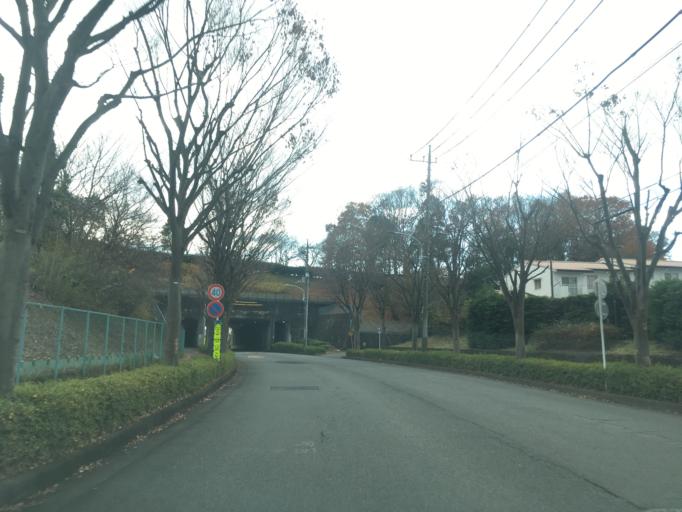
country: JP
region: Tokyo
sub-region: Machida-shi
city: Machida
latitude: 35.5869
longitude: 139.4061
